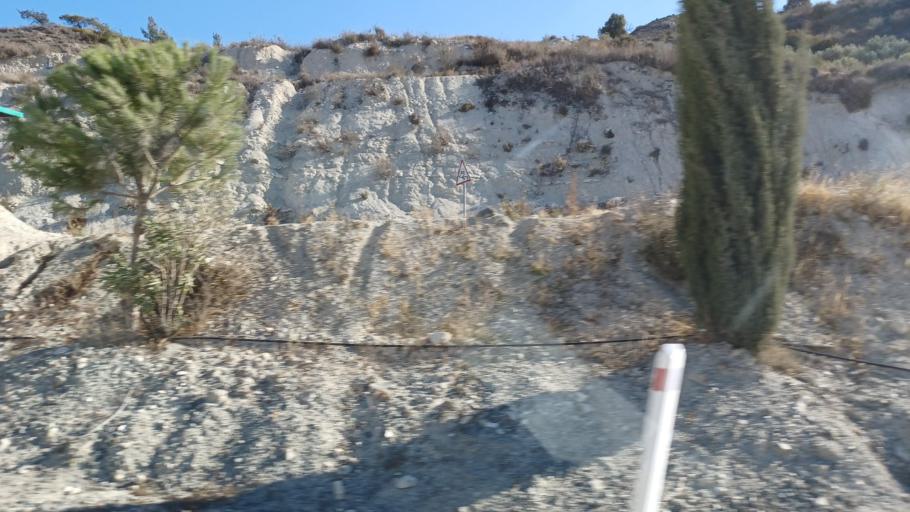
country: CY
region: Limassol
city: Pyrgos
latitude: 34.7702
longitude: 33.2418
